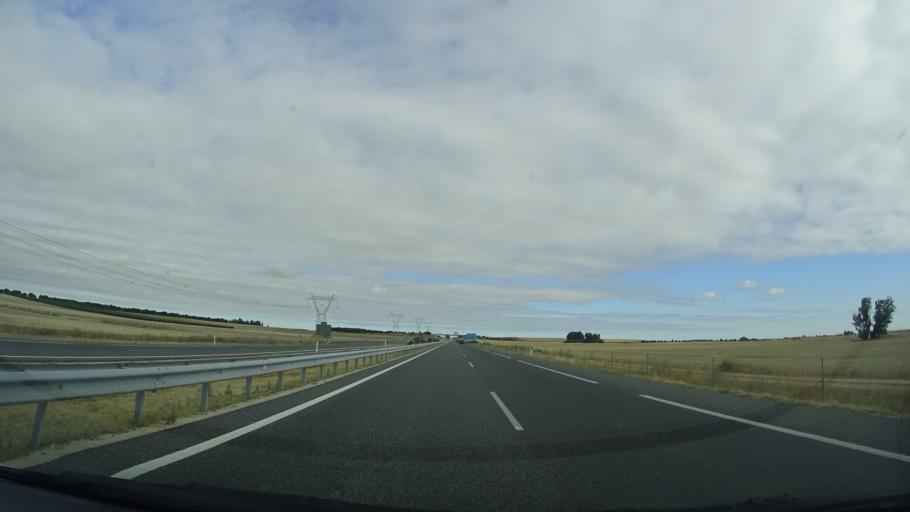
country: ES
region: Castille and Leon
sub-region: Provincia de Valladolid
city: San Pablo de la Moraleja
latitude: 41.1403
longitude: -4.7820
